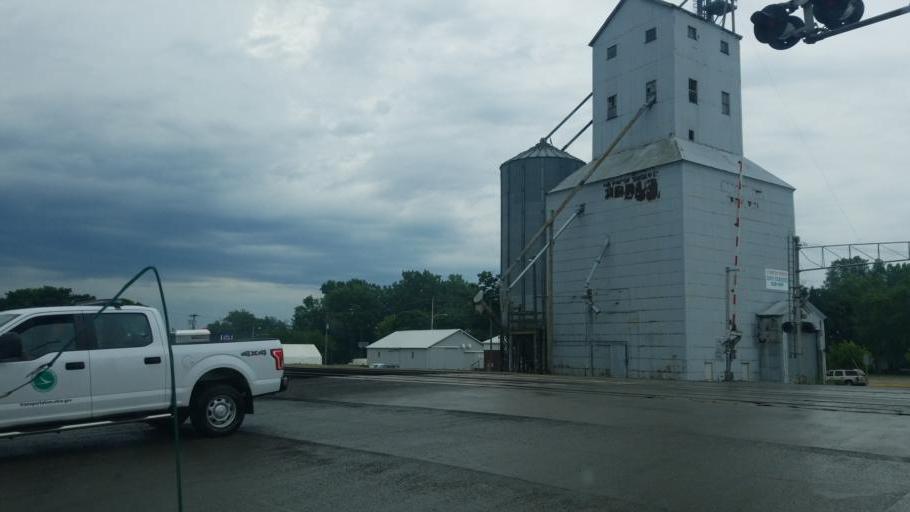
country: US
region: Ohio
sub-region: Williams County
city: Edgerton
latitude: 41.4487
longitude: -84.7432
